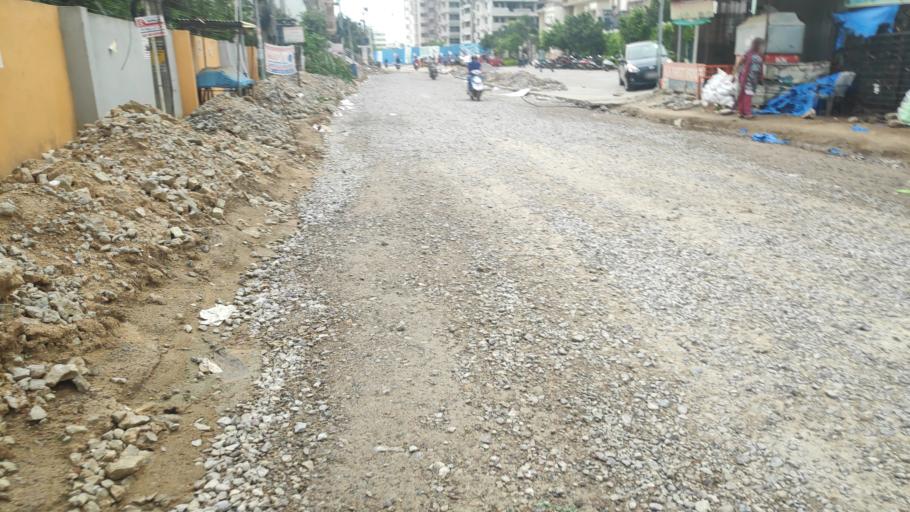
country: IN
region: Telangana
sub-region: Rangareddi
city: Kukatpalli
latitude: 17.5134
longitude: 78.3871
